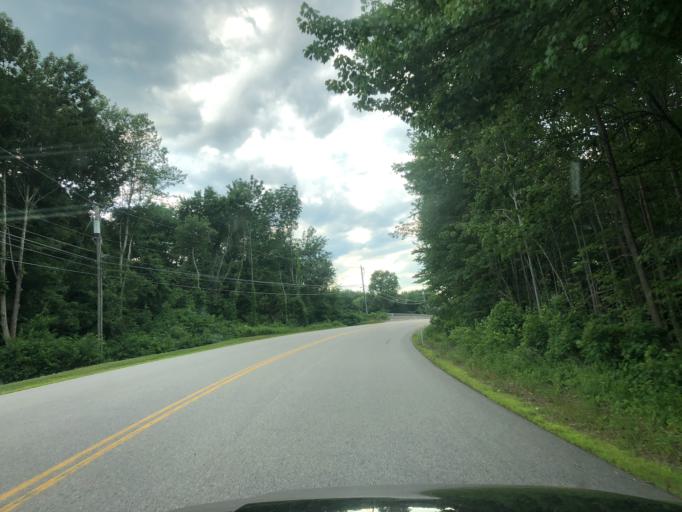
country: US
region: Connecticut
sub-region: New London County
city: Colchester
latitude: 41.5697
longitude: -72.3008
